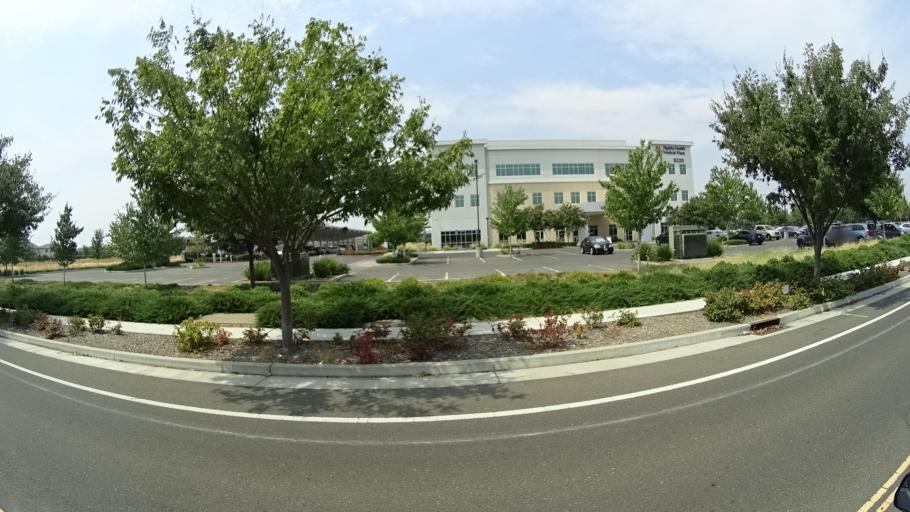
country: US
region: California
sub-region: Sacramento County
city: Laguna
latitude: 38.4066
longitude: -121.4090
